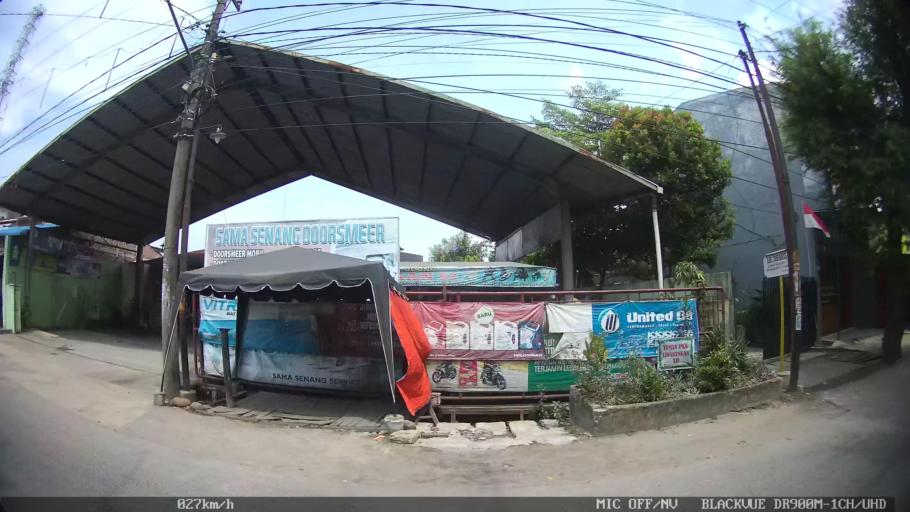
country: ID
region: North Sumatra
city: Labuhan Deli
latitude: 3.6588
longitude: 98.6772
